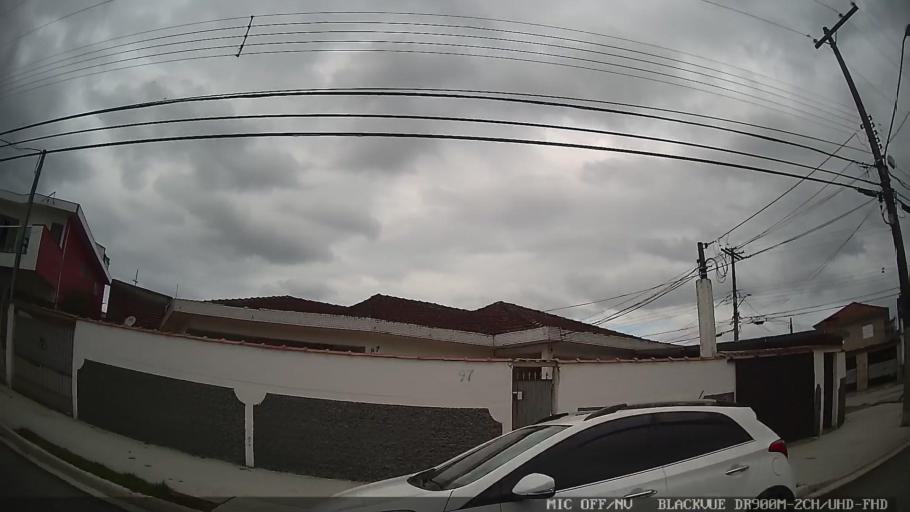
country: BR
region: Sao Paulo
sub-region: Guaruja
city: Guaruja
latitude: -23.9947
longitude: -46.2863
